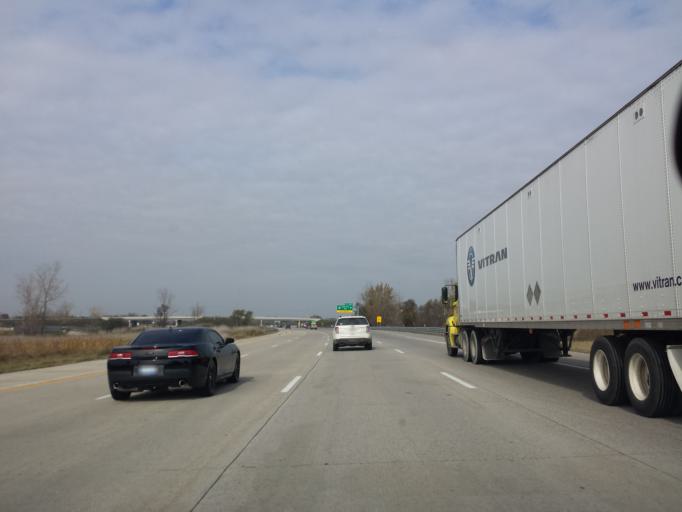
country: US
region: Michigan
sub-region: Bay County
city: Bay City
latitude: 43.5559
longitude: -83.9454
